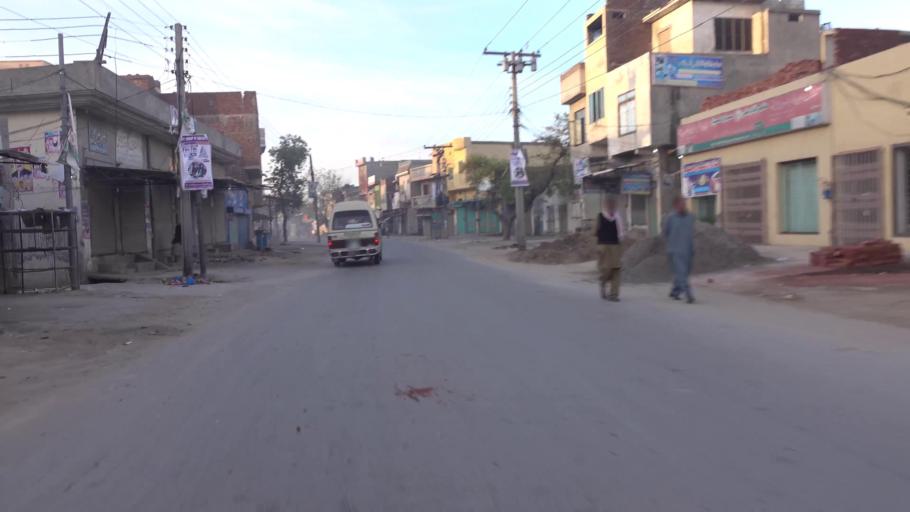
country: PK
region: Punjab
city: Hafizabad
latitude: 32.0676
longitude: 73.6888
